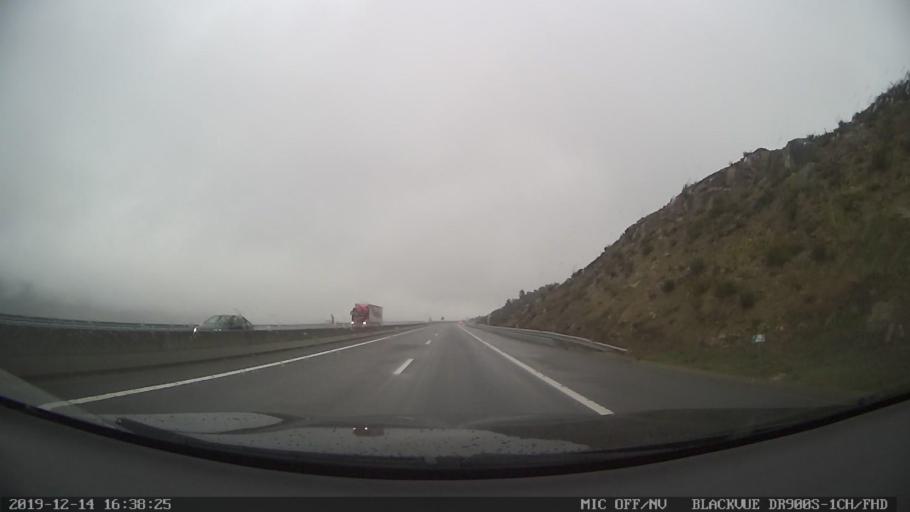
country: PT
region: Vila Real
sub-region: Sabrosa
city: Sabrosa
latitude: 41.3685
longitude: -7.5560
